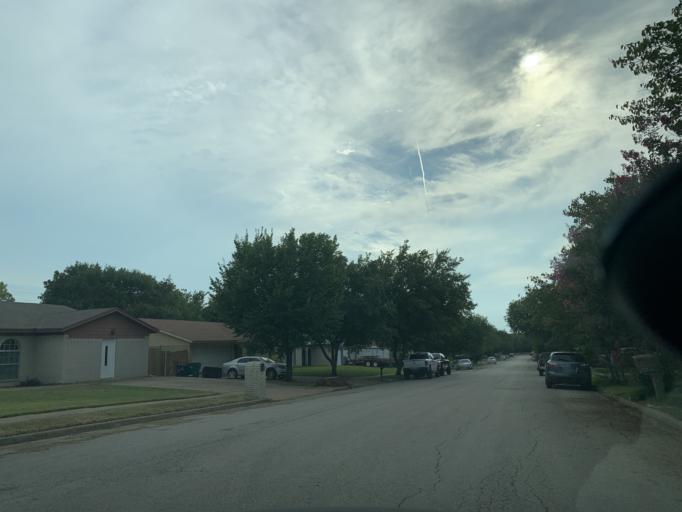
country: US
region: Texas
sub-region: Tarrant County
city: Watauga
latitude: 32.8723
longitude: -97.2394
